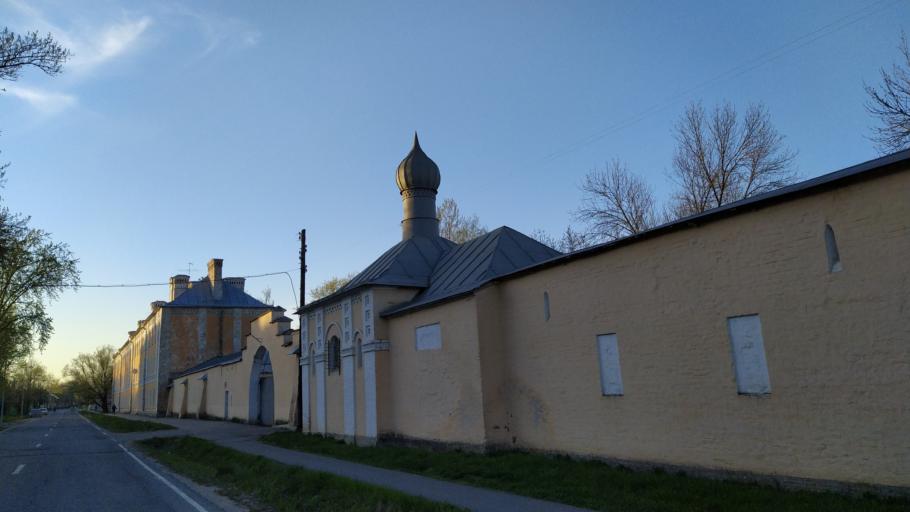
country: RU
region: St.-Petersburg
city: Pushkin
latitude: 59.7025
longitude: 30.3978
